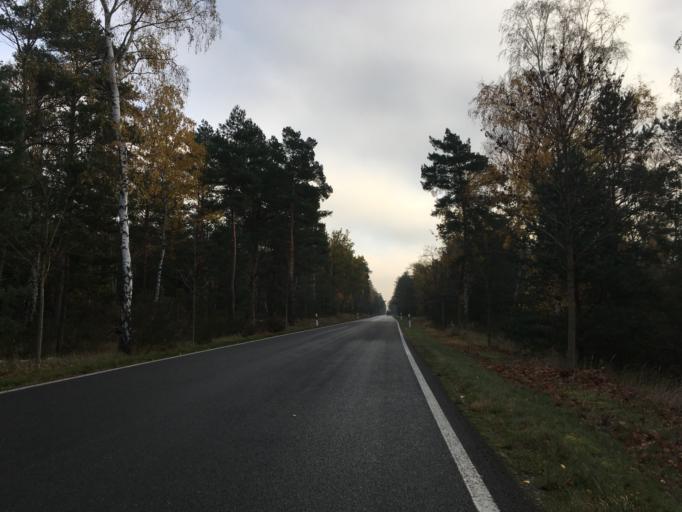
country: DE
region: Brandenburg
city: Halbe
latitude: 52.0326
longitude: 13.7649
